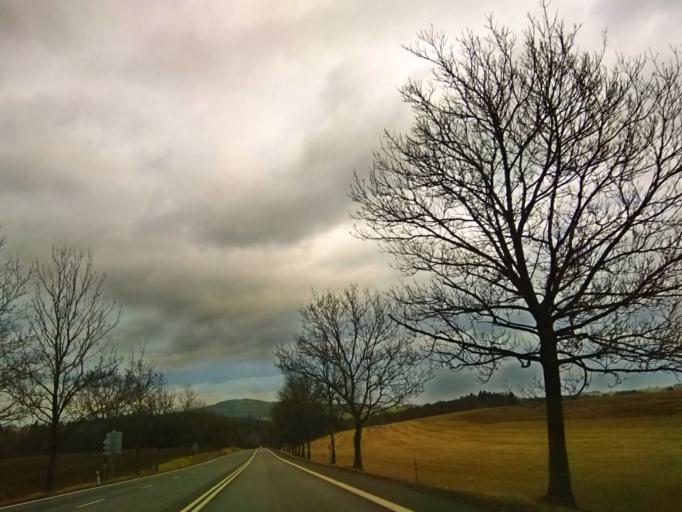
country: CZ
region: Jihocesky
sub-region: Okres Cesky Krumlov
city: Cesky Krumlov
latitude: 48.8359
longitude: 14.3494
